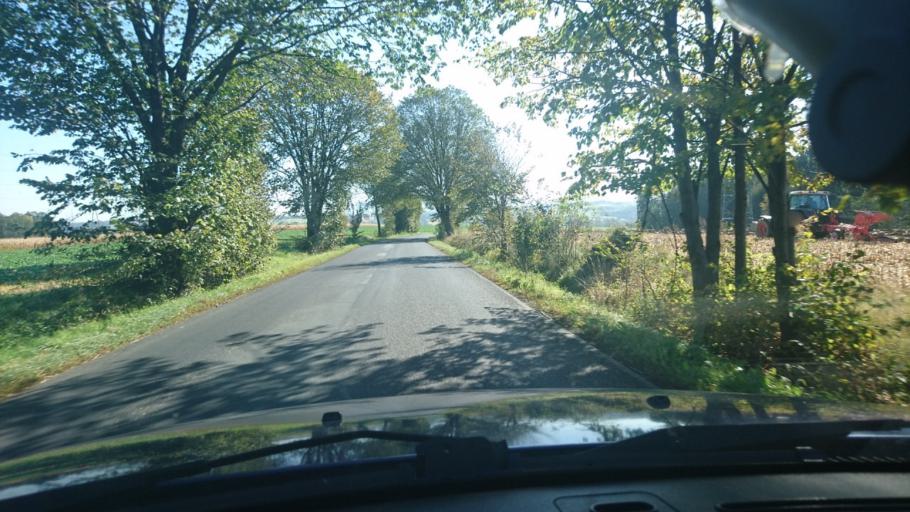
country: PL
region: Silesian Voivodeship
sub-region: Powiat bielski
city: Bronow
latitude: 49.8560
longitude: 18.9236
